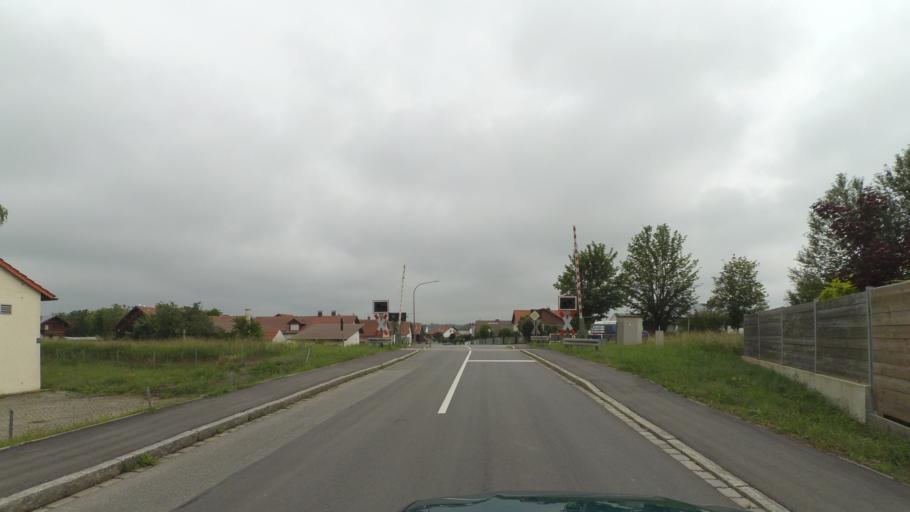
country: DE
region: Bavaria
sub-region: Lower Bavaria
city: Geiselhoring
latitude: 48.8211
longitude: 12.3889
